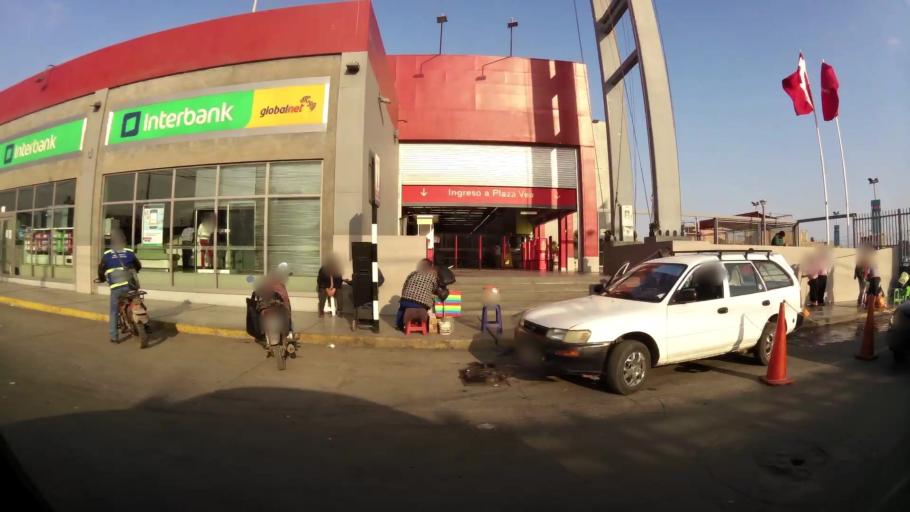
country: PE
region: La Libertad
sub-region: Provincia de Trujillo
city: El Porvenir
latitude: -8.0905
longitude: -79.0067
